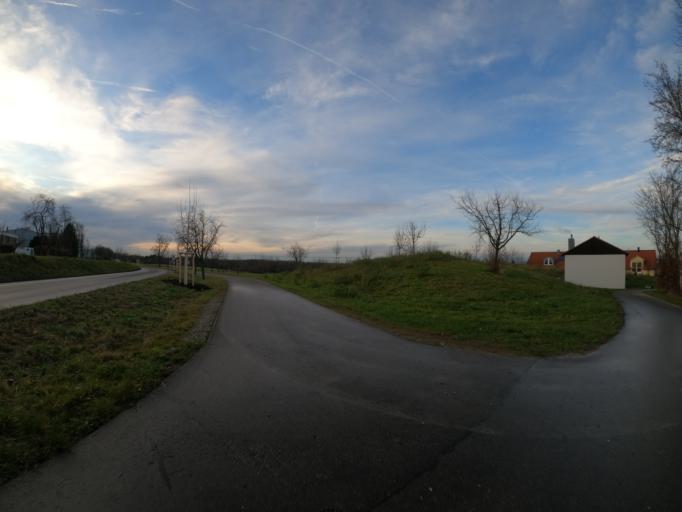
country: DE
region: Baden-Wuerttemberg
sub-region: Regierungsbezirk Stuttgart
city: Hattenhofen
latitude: 48.6661
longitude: 9.5581
